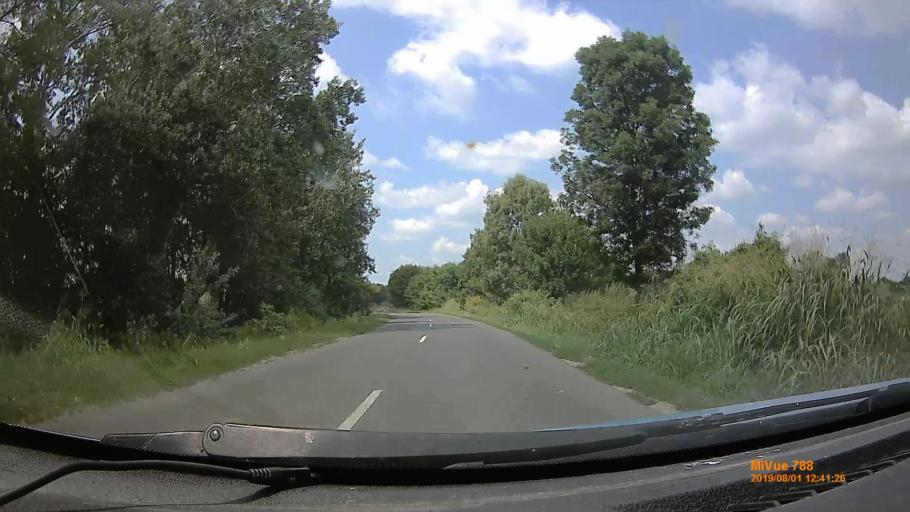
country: HU
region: Baranya
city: Harkany
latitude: 45.8363
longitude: 18.1757
